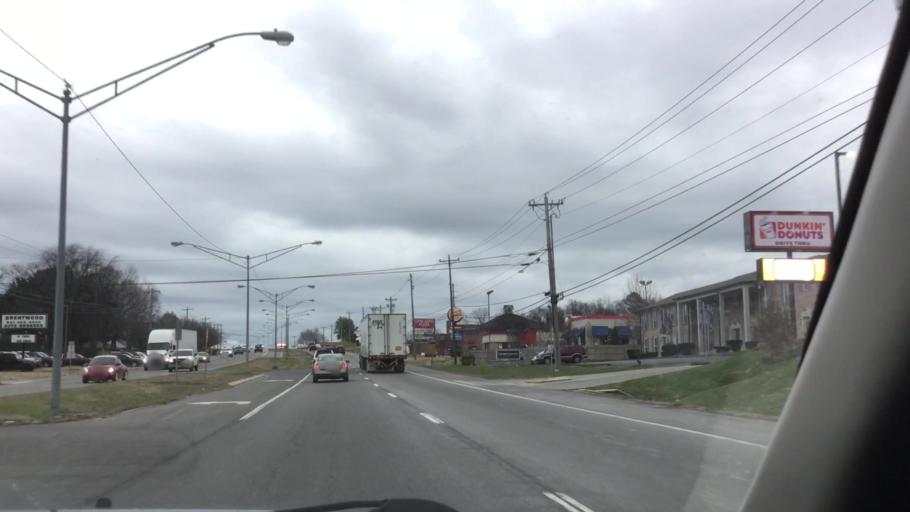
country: US
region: Tennessee
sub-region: Maury County
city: Columbia
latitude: 35.6381
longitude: -87.0160
